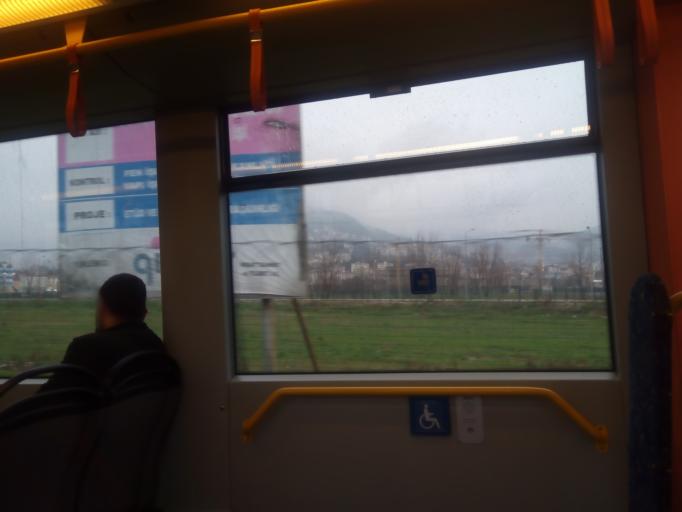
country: TR
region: Bursa
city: Yildirim
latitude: 40.2131
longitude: 29.0116
